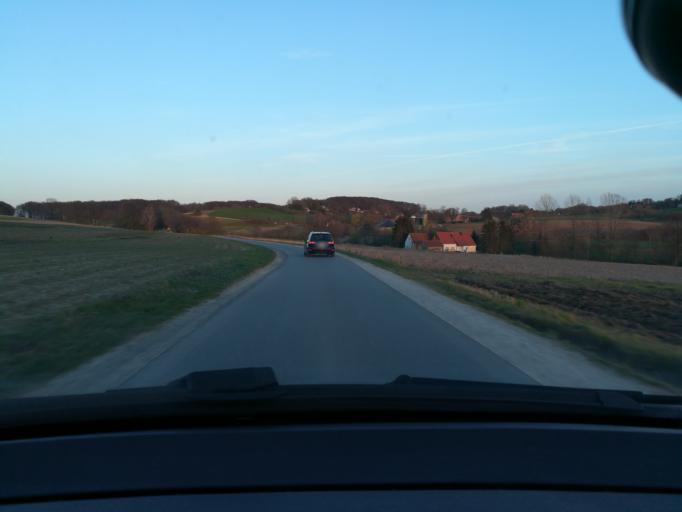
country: DE
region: North Rhine-Westphalia
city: Halle
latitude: 52.0911
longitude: 8.3441
